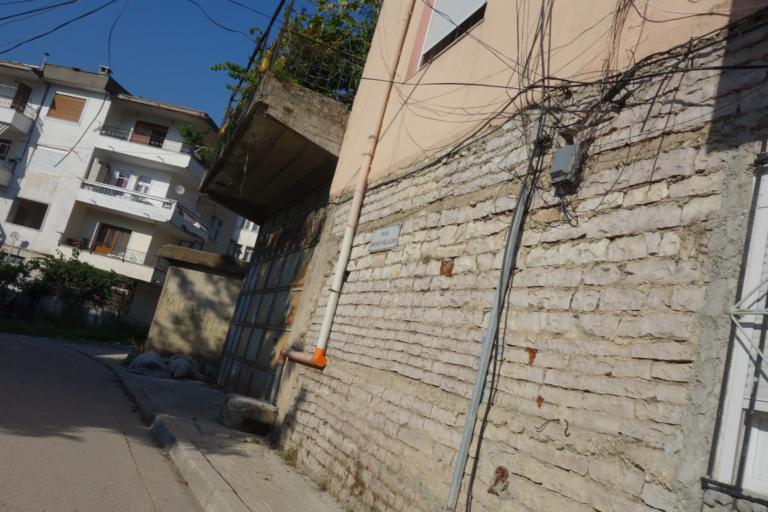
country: AL
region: Gjirokaster
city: Gjirokaster
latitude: 40.0785
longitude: 20.1478
